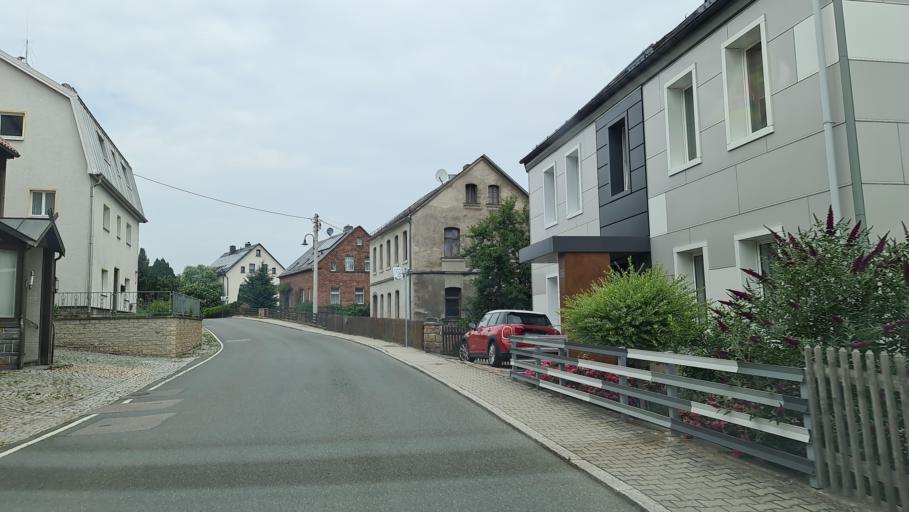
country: DE
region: Saxony
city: Hirschfeld
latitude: 50.6246
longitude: 12.4610
